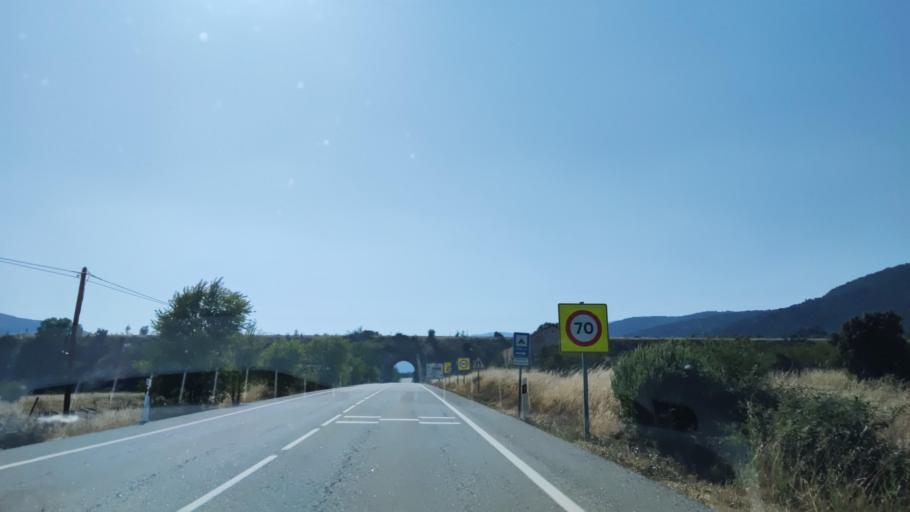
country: ES
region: Madrid
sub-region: Provincia de Madrid
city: Canencia
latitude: 40.9443
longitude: -3.7211
